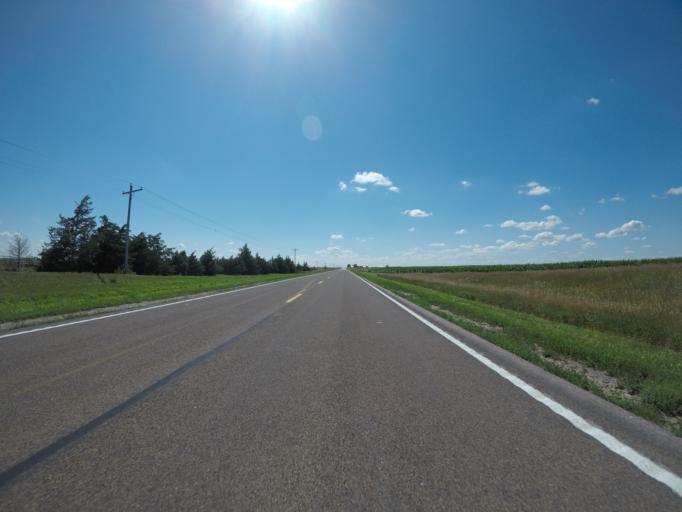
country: US
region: Nebraska
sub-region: Chase County
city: Imperial
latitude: 40.5376
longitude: -101.8403
